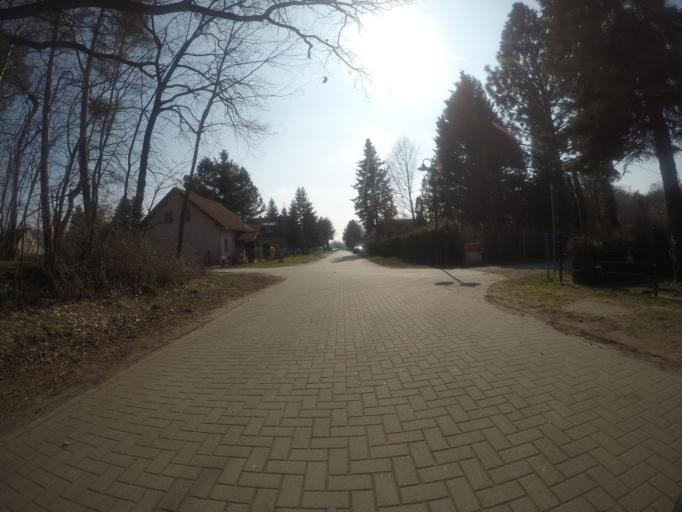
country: DE
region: Brandenburg
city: Bestensee
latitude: 52.2874
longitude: 13.7479
